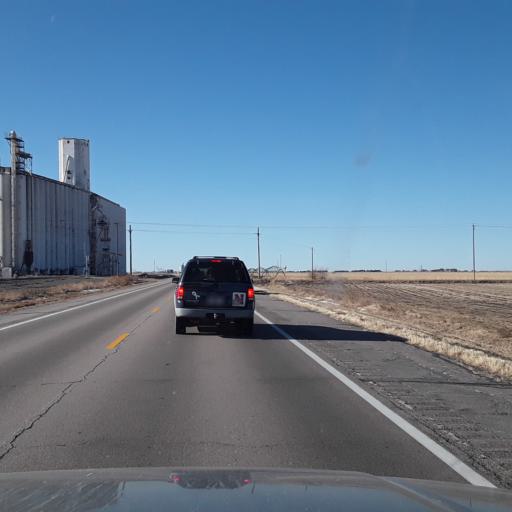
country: US
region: Nebraska
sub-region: Kearney County
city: Minden
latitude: 40.4923
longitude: -99.0259
